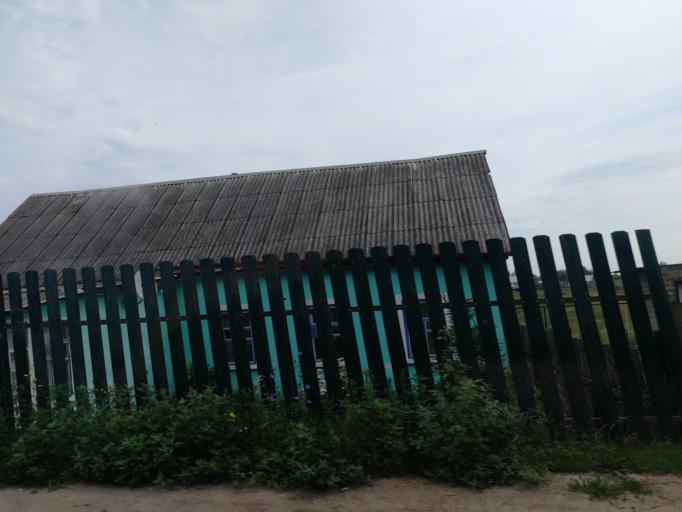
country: RU
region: Tula
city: Tovarkovskiy
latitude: 53.6966
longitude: 38.1659
